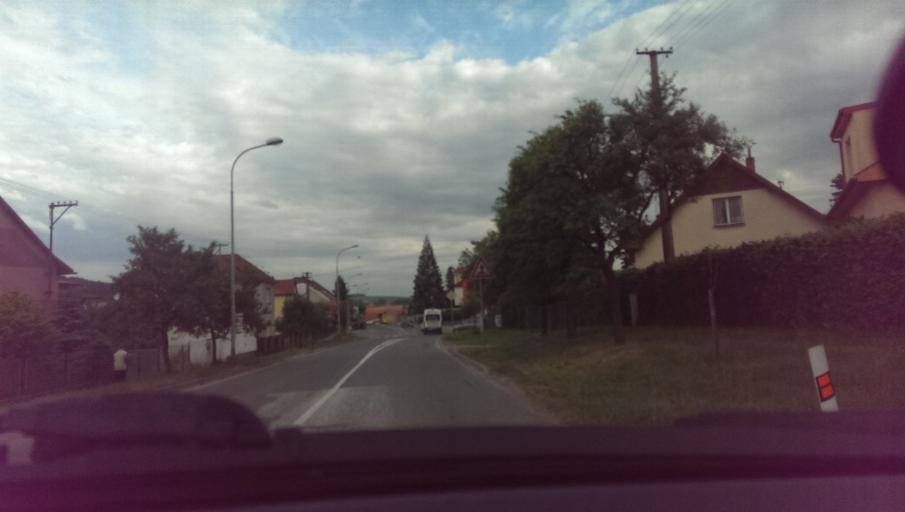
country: CZ
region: Zlin
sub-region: Okres Zlin
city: Napajedla
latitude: 49.1644
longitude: 17.5156
